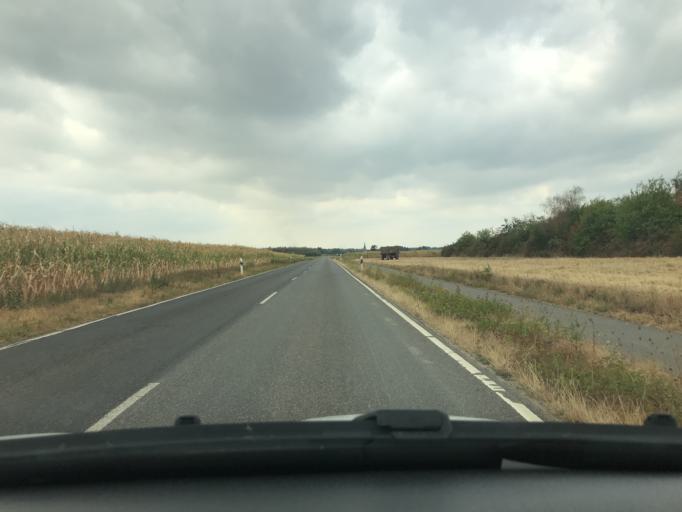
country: DE
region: North Rhine-Westphalia
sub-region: Regierungsbezirk Dusseldorf
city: Dormagen
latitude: 51.0984
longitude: 6.7871
